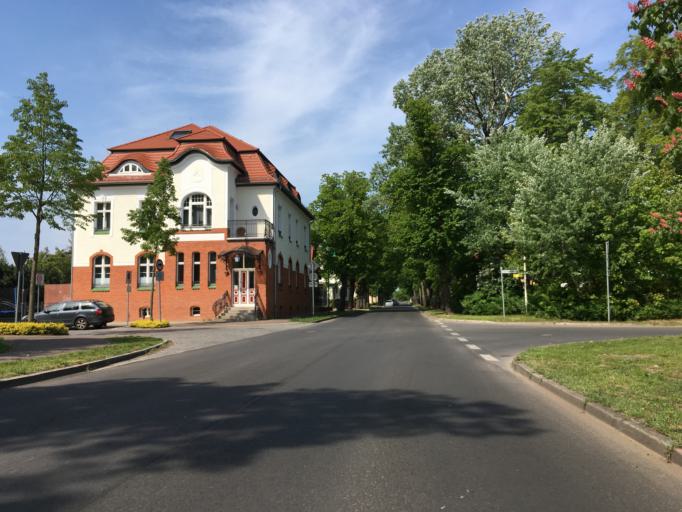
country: DE
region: Brandenburg
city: Werneuchen
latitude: 52.6338
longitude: 13.7381
